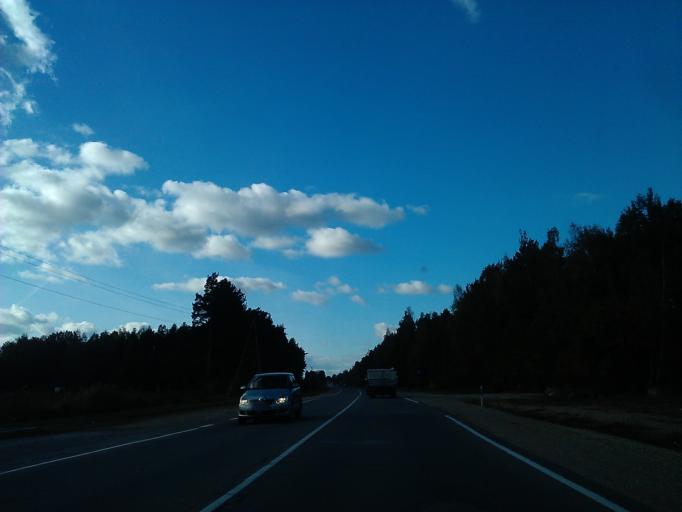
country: LV
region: Koknese
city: Koknese
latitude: 56.6144
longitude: 25.4949
